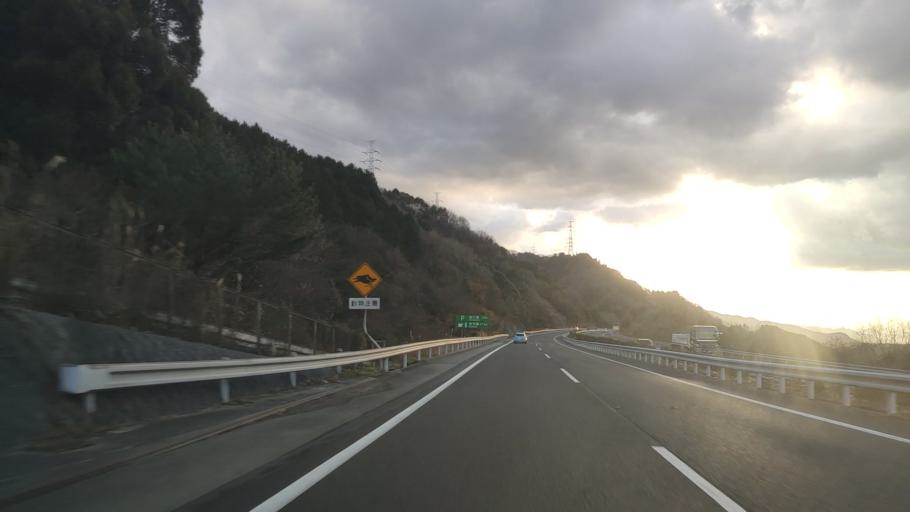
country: JP
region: Ehime
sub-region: Shikoku-chuo Shi
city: Matsuyama
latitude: 33.8151
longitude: 132.9568
